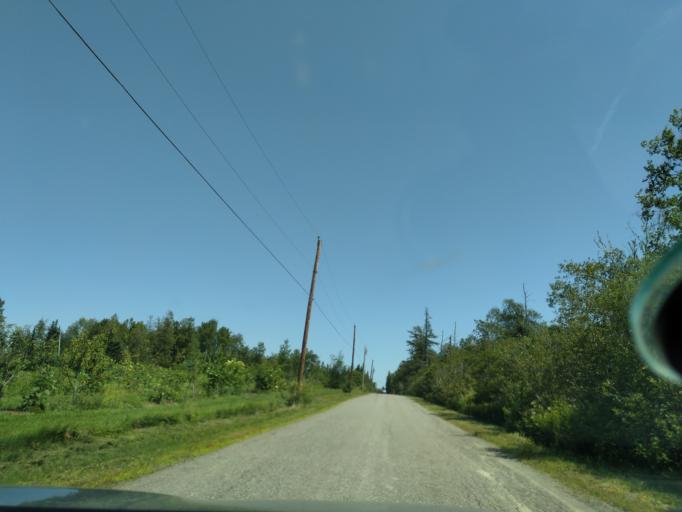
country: US
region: Maine
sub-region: Washington County
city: Eastport
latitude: 44.8313
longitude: -66.9977
